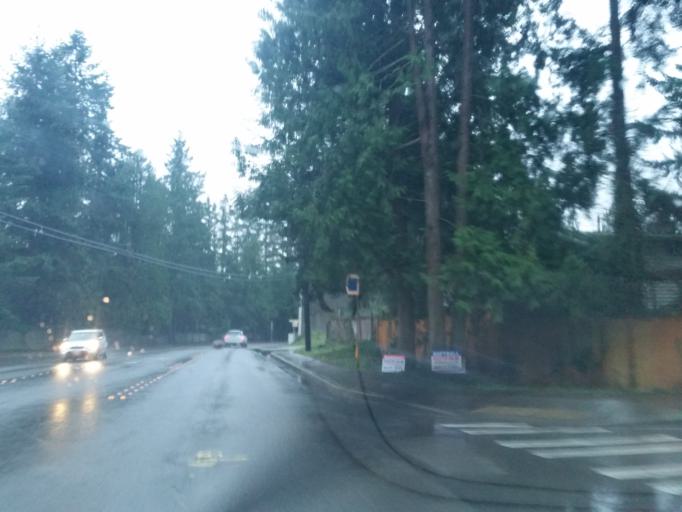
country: US
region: Washington
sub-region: Snohomish County
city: Meadowdale
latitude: 47.8449
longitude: -122.3194
